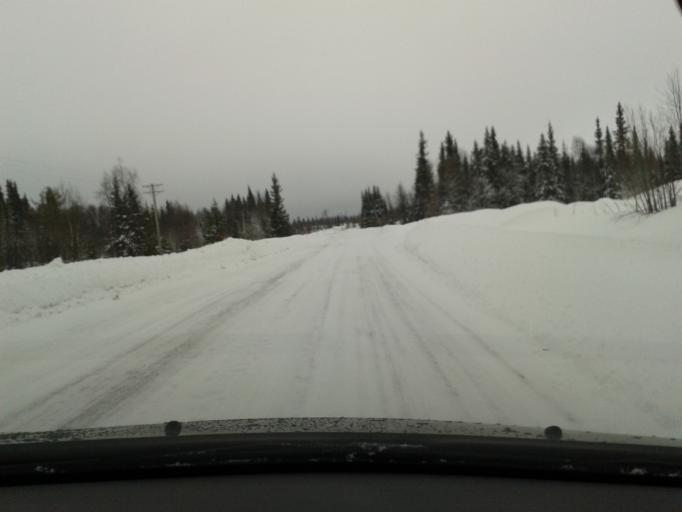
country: SE
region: Vaesterbotten
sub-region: Vilhelmina Kommun
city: Sjoberg
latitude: 65.1495
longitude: 15.8643
